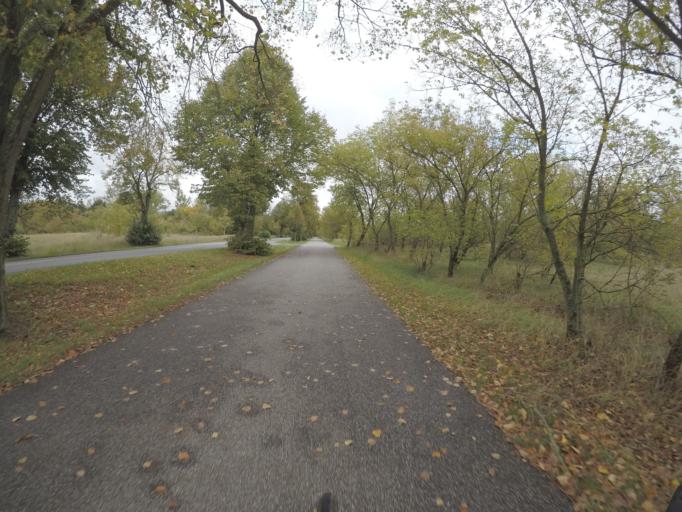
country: DE
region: Berlin
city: Buch
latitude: 52.6612
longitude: 13.4925
